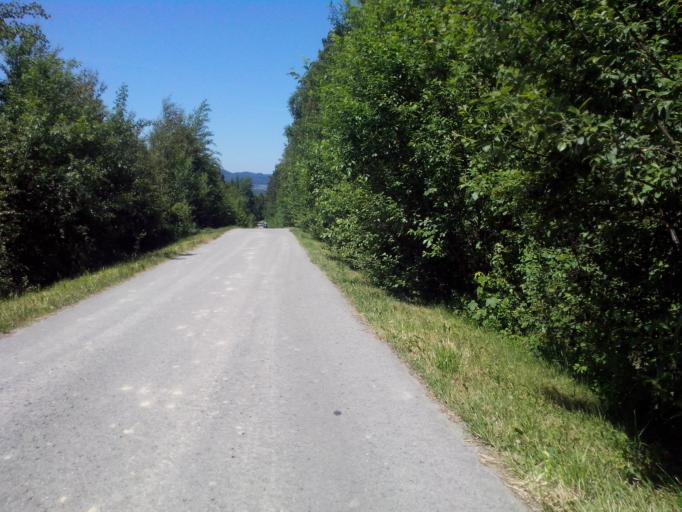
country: PL
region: Subcarpathian Voivodeship
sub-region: Powiat strzyzowski
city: Wysoka Strzyzowska
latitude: 49.8130
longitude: 21.7830
